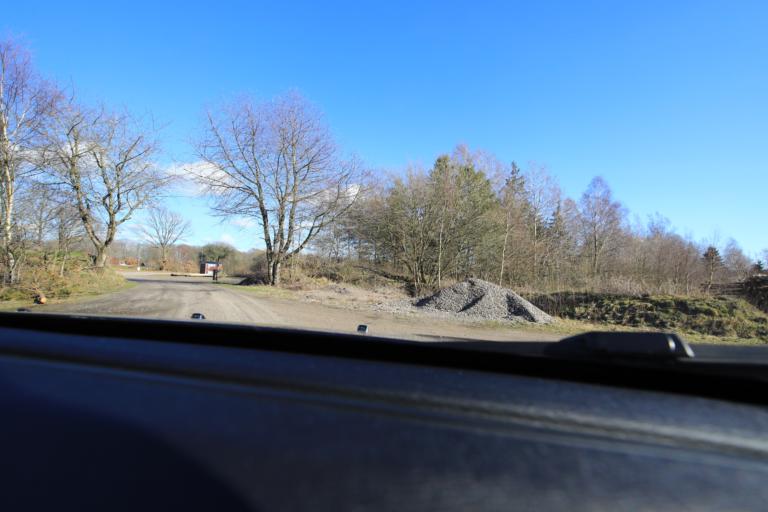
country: SE
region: Halland
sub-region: Varbergs Kommun
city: Tvaaker
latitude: 57.0704
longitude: 12.4687
